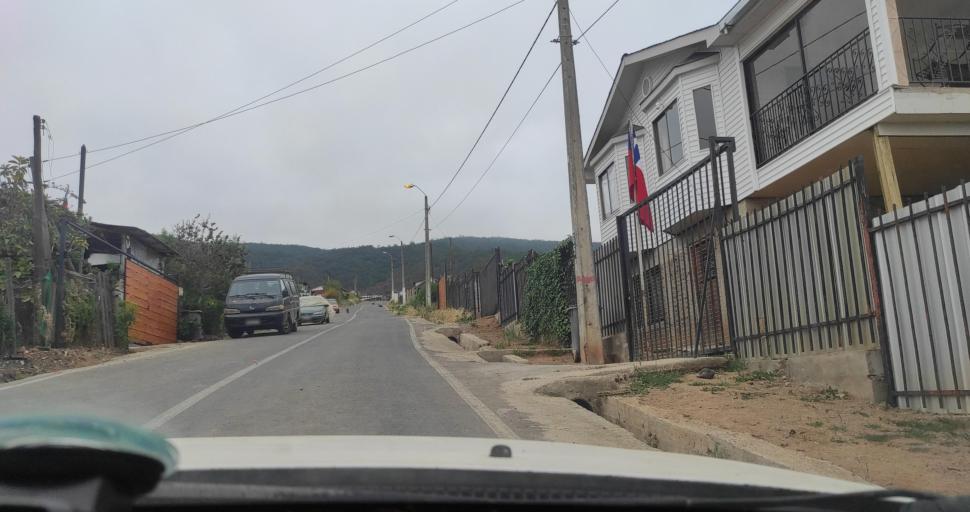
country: CL
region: Valparaiso
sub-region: Provincia de Marga Marga
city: Limache
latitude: -32.9847
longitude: -71.2266
